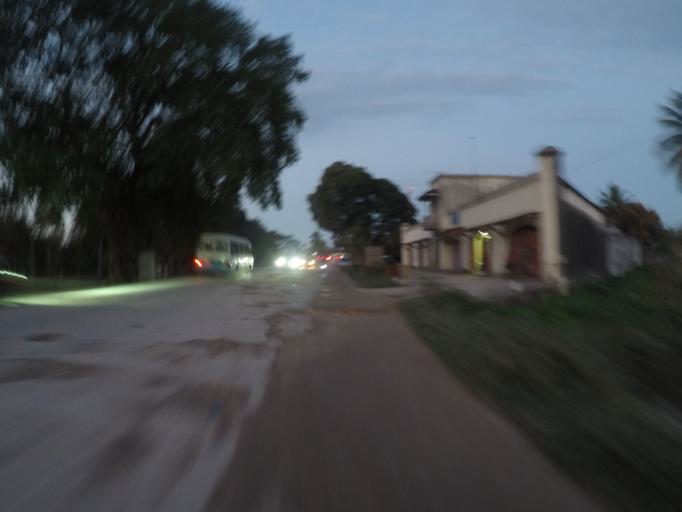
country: TZ
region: Zanzibar Central/South
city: Koani
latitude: -6.0911
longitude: 39.2203
